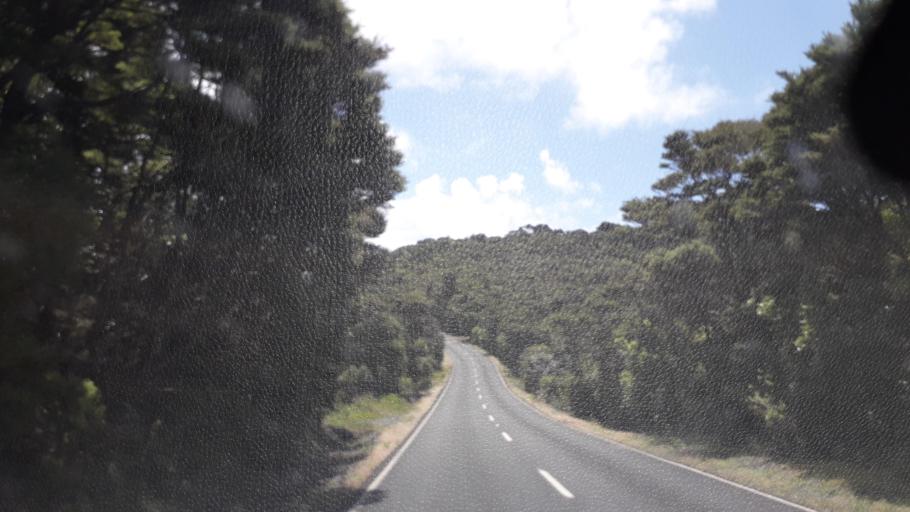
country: NZ
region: Northland
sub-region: Far North District
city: Paihia
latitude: -35.2487
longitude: 174.2587
